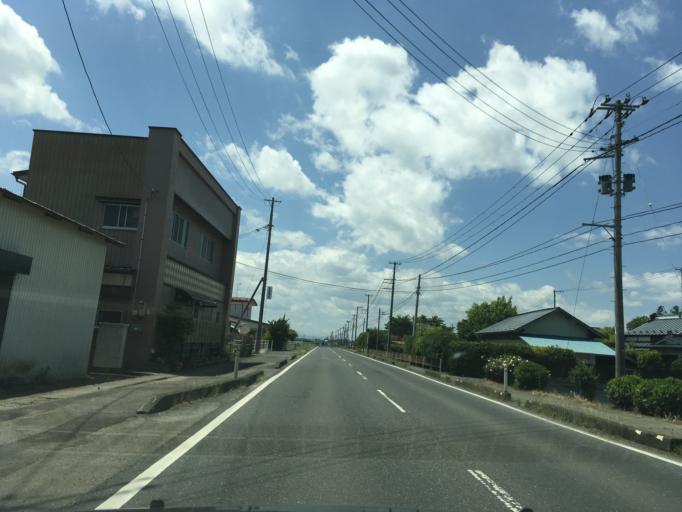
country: JP
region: Miyagi
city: Wakuya
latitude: 38.6774
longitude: 141.2406
